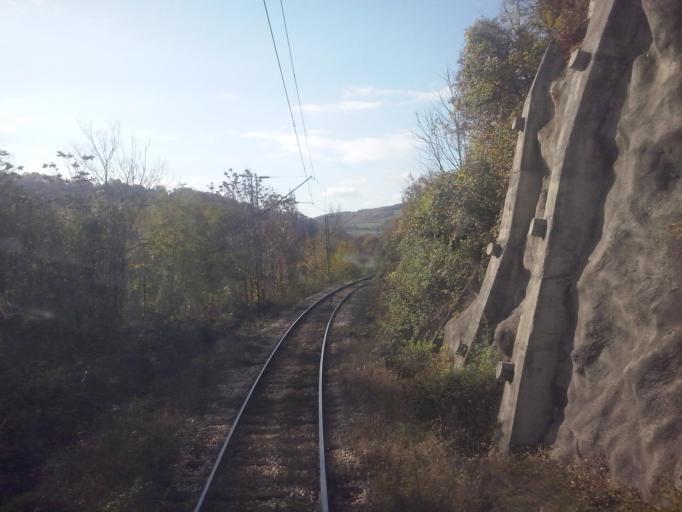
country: RS
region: Central Serbia
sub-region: Kolubarski Okrug
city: Valjevo
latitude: 44.2595
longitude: 19.8916
